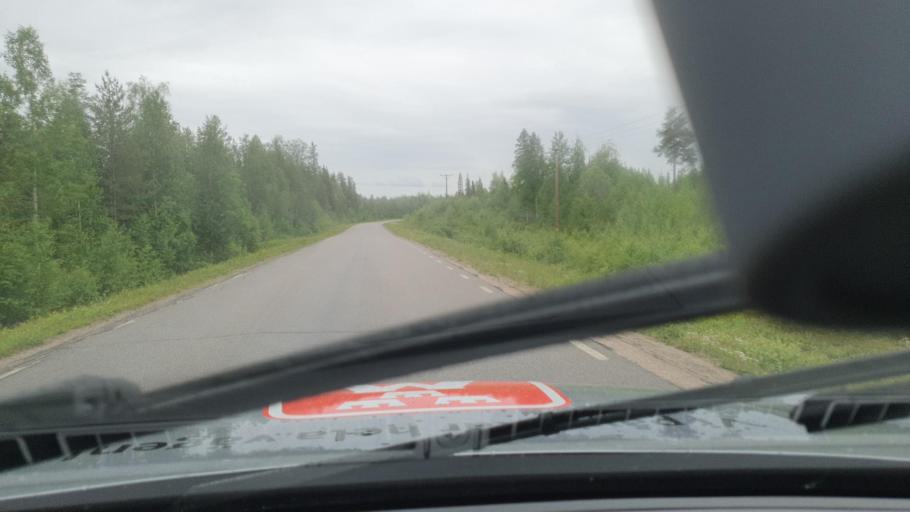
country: SE
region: Norrbotten
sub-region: Pajala Kommun
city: Pajala
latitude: 66.7485
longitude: 23.1663
